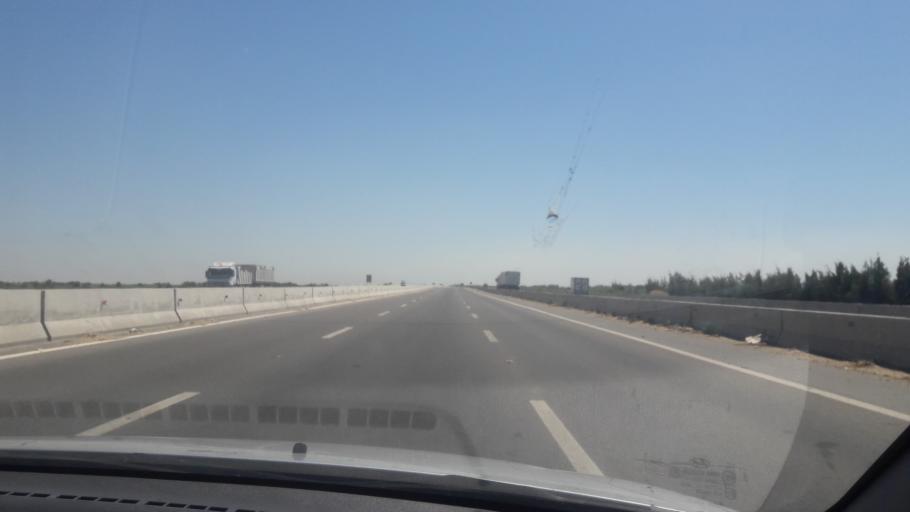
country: EG
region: Muhafazat ad Daqahliyah
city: Al Matariyah
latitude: 30.9080
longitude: 32.1857
